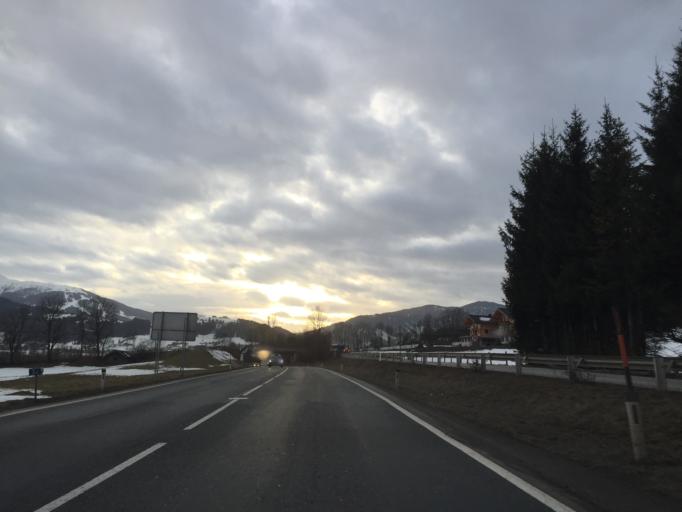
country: AT
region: Salzburg
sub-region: Politischer Bezirk Sankt Johann im Pongau
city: Radstadt
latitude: 47.3867
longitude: 13.4502
